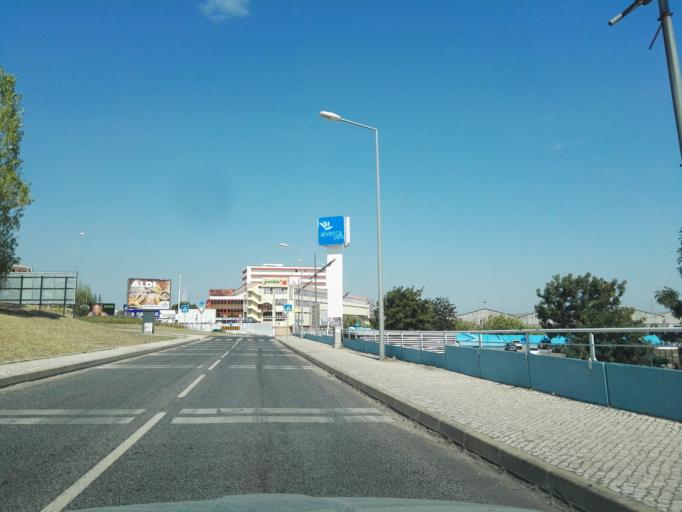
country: PT
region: Lisbon
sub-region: Vila Franca de Xira
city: Vialonga
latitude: 38.8864
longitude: -9.0465
